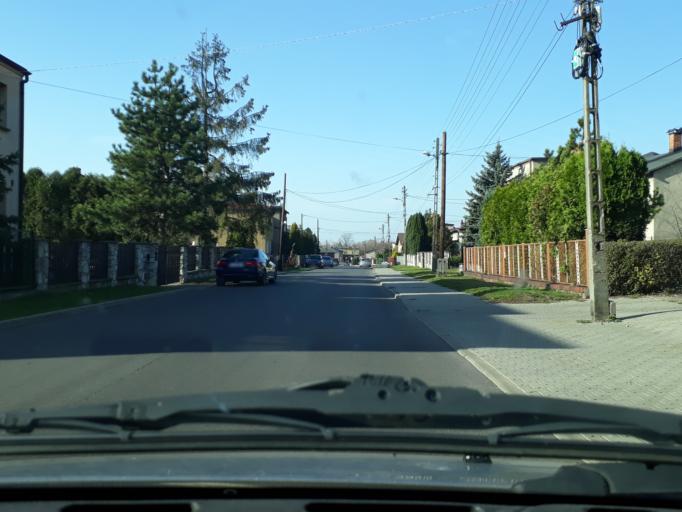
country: PL
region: Silesian Voivodeship
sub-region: Powiat tarnogorski
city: Radzionkow
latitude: 50.4217
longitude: 18.8810
